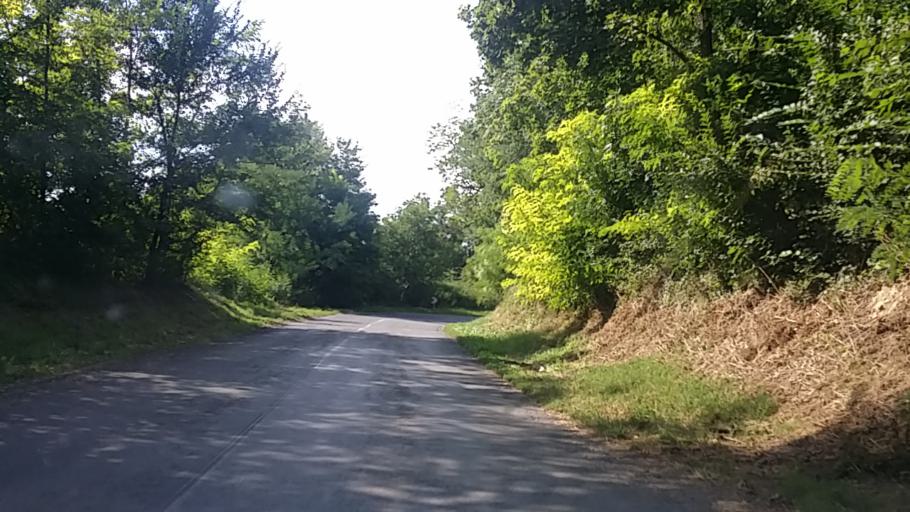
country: HU
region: Tolna
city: Gyonk
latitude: 46.5384
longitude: 18.4757
